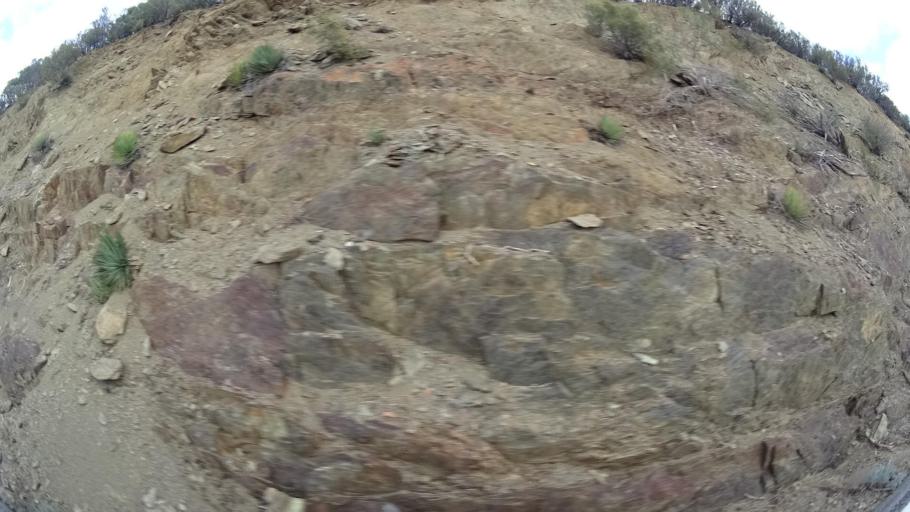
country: US
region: California
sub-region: San Diego County
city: Pine Valley
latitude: 32.8318
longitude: -116.4962
